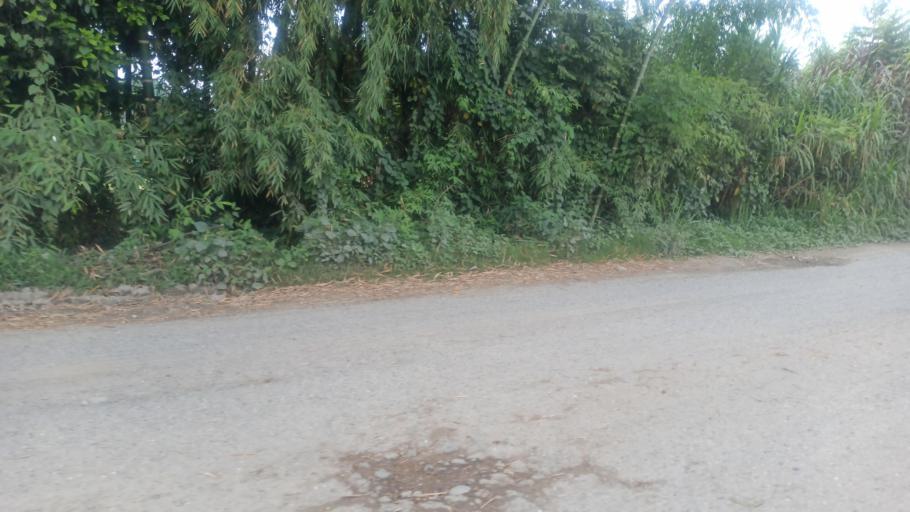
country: CO
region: Valle del Cauca
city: Jamundi
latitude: 3.2015
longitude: -76.5014
